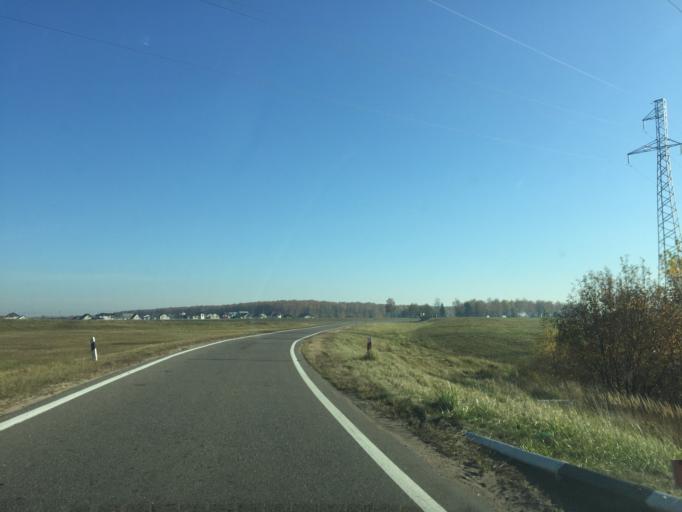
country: BY
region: Mogilev
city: Buynichy
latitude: 53.9469
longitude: 30.2205
